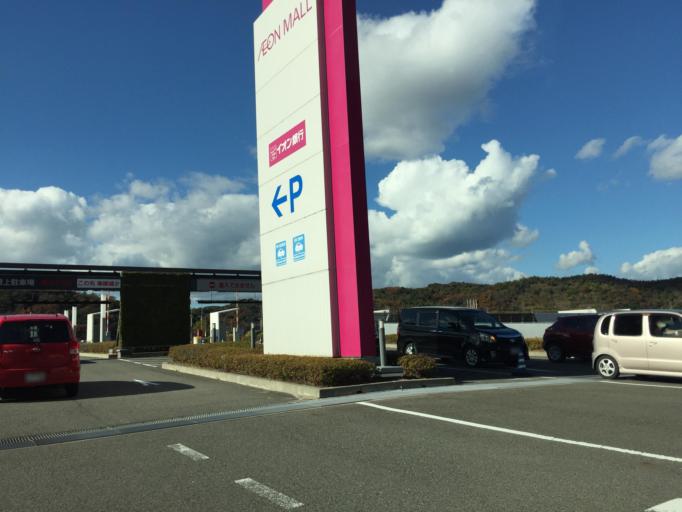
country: JP
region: Wakayama
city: Wakayama-shi
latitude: 34.2757
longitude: 135.1506
